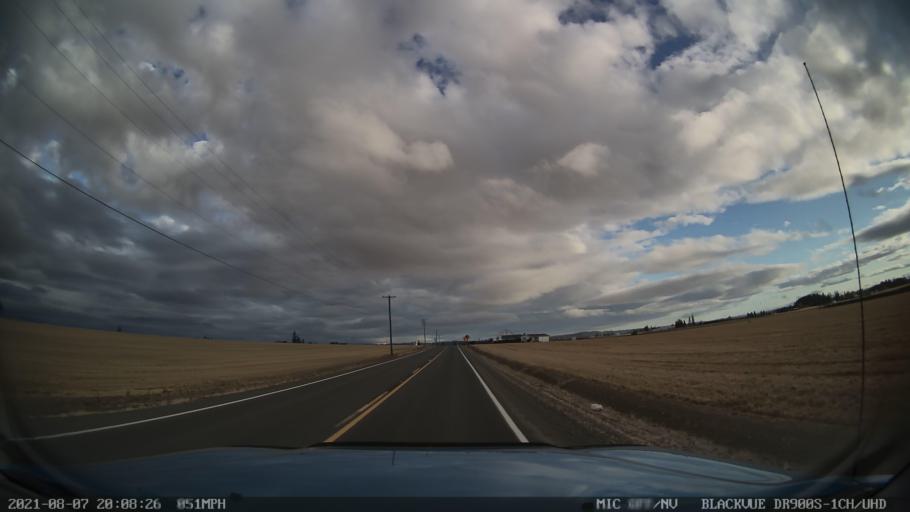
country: US
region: Oregon
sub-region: Marion County
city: Silverton
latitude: 44.9807
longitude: -122.8805
